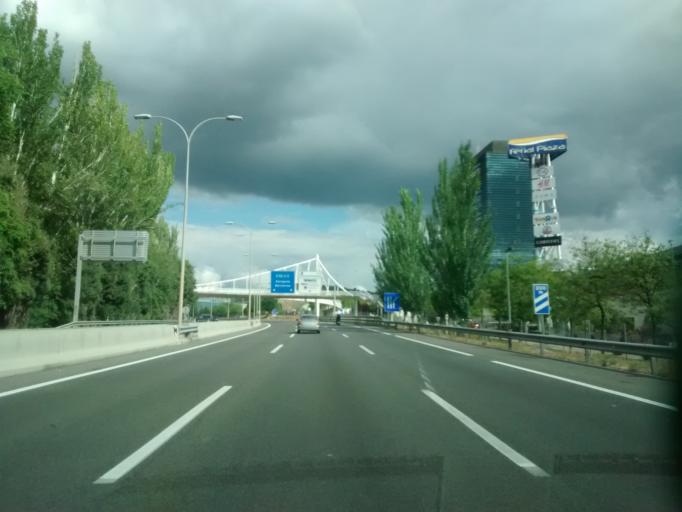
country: ES
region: Castille-La Mancha
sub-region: Provincia de Guadalajara
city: Guadalajara
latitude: 40.6232
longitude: -3.1656
